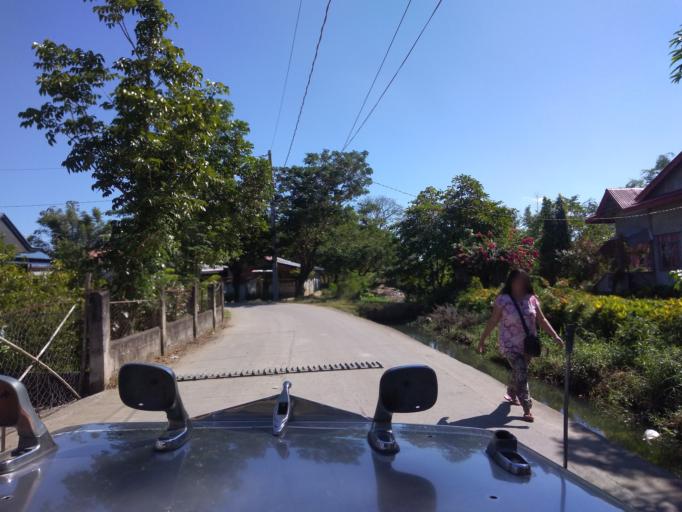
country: PH
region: Central Luzon
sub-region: Province of Pampanga
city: Batasan Bata
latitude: 15.1659
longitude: 120.9180
